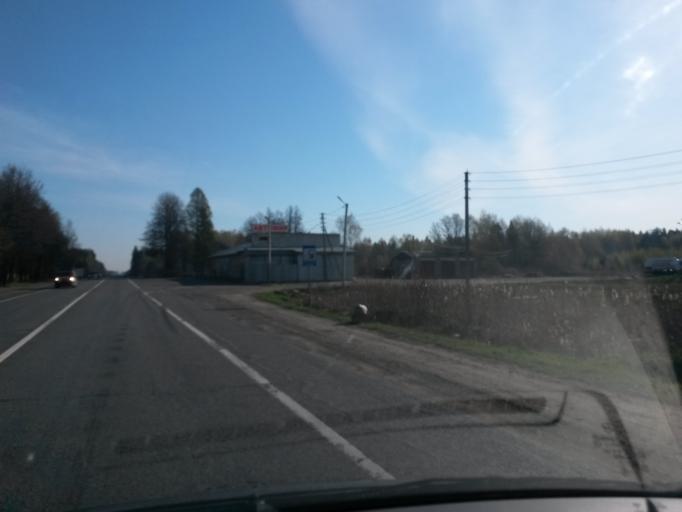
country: RU
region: Jaroslavl
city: Petrovsk
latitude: 56.8980
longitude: 39.1079
